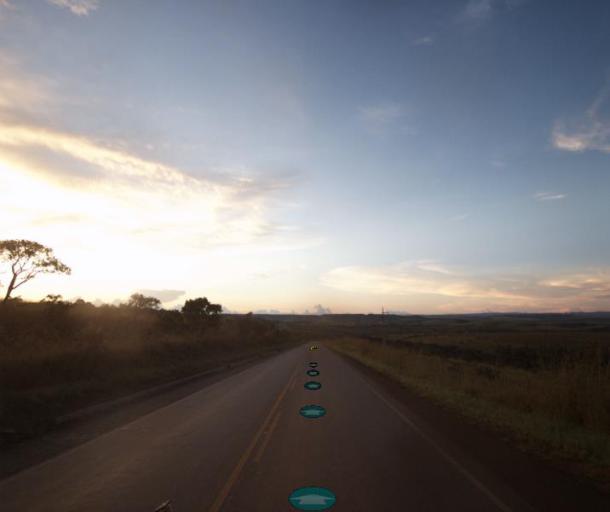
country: BR
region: Goias
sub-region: Pirenopolis
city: Pirenopolis
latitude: -16.0130
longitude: -48.8390
